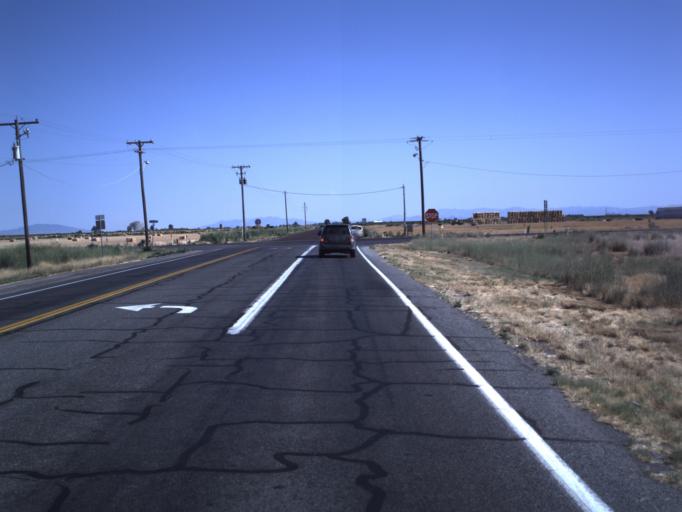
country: US
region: Utah
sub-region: Millard County
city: Delta
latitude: 39.3299
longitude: -112.6522
